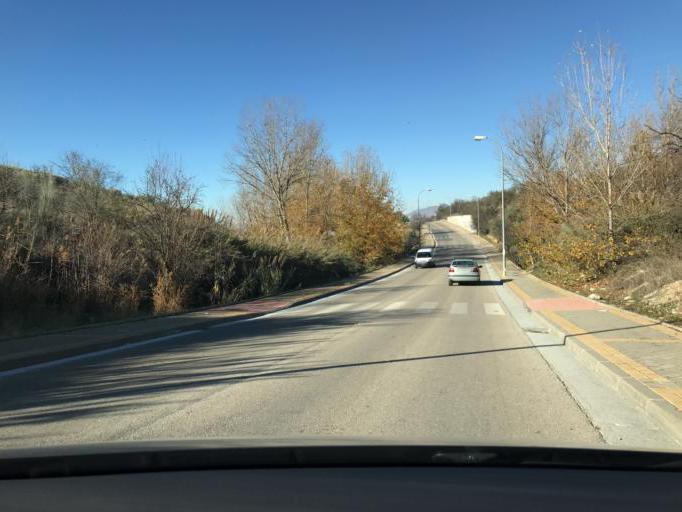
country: ES
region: Andalusia
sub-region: Provincia de Granada
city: Jun
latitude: 37.2185
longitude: -3.5799
